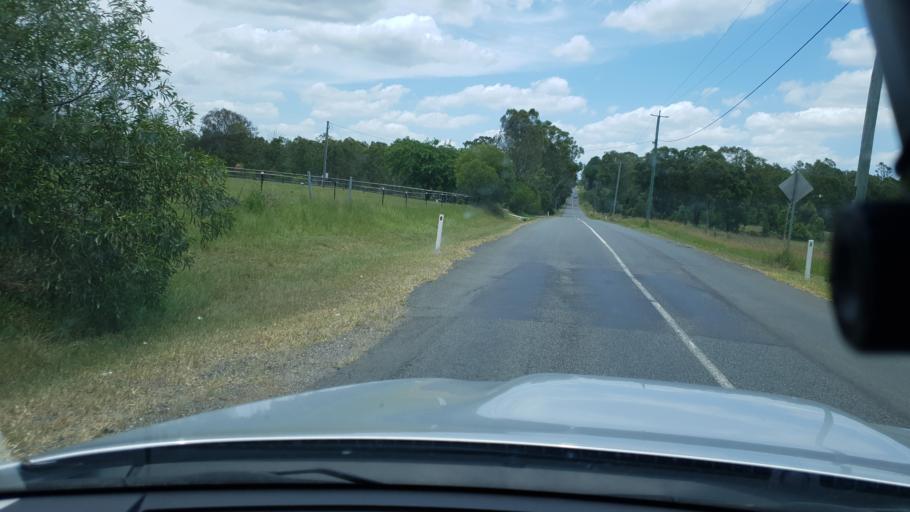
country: AU
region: Queensland
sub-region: Logan
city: North Maclean
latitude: -27.7731
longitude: 152.9981
